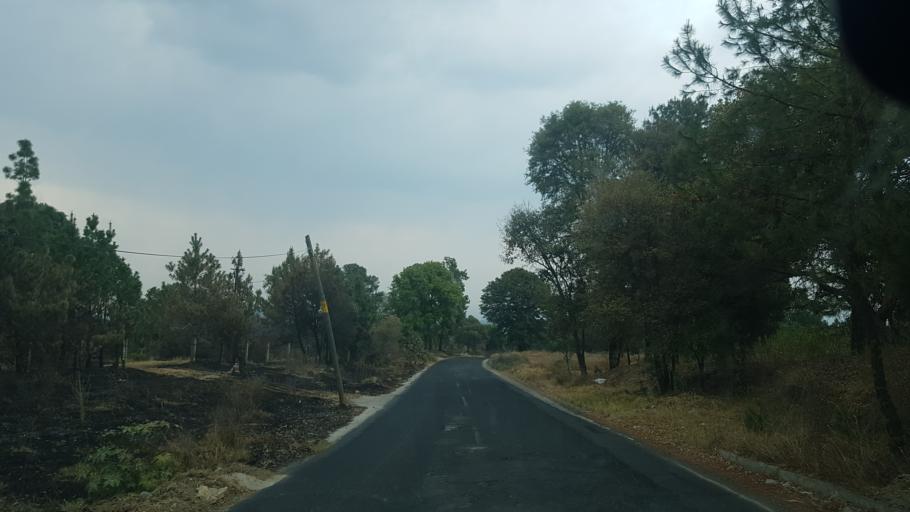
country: MX
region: Puebla
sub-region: Chiautzingo
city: San Nicolas Zecalacoayan
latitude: 19.1884
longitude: -98.4761
